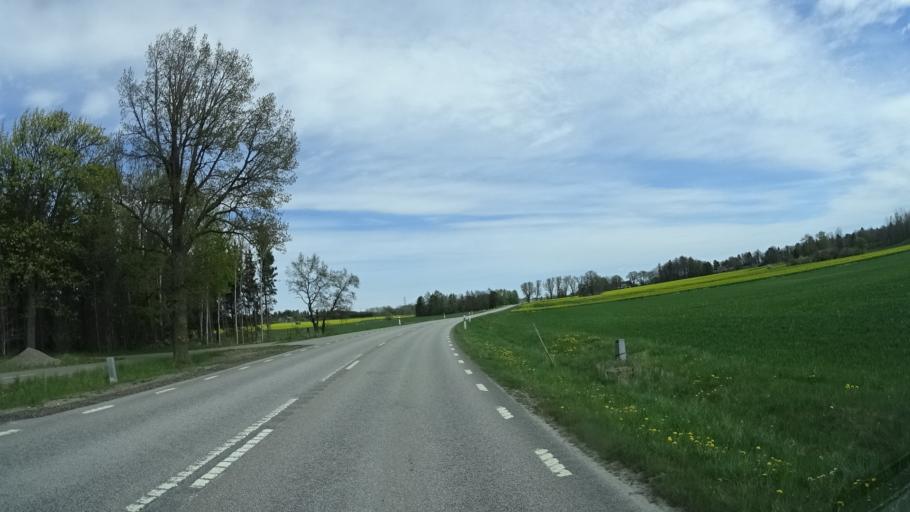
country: SE
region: OEstergoetland
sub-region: Linkopings Kommun
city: Vikingstad
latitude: 58.3713
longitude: 15.3918
